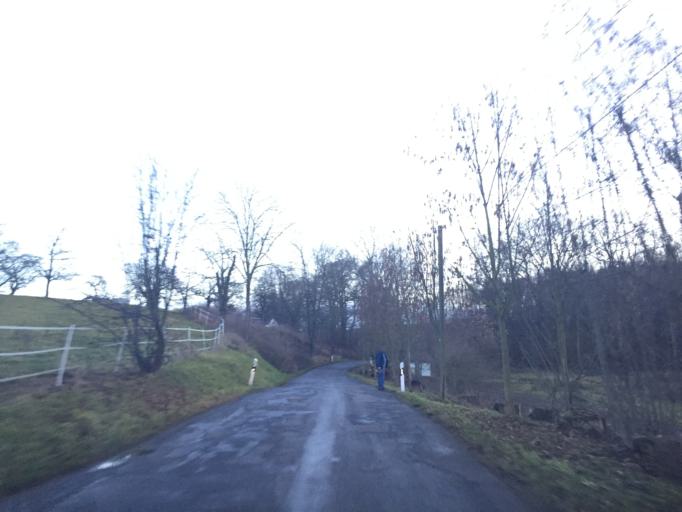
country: DE
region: Thuringia
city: Heyersdorf
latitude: 50.8730
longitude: 12.3328
